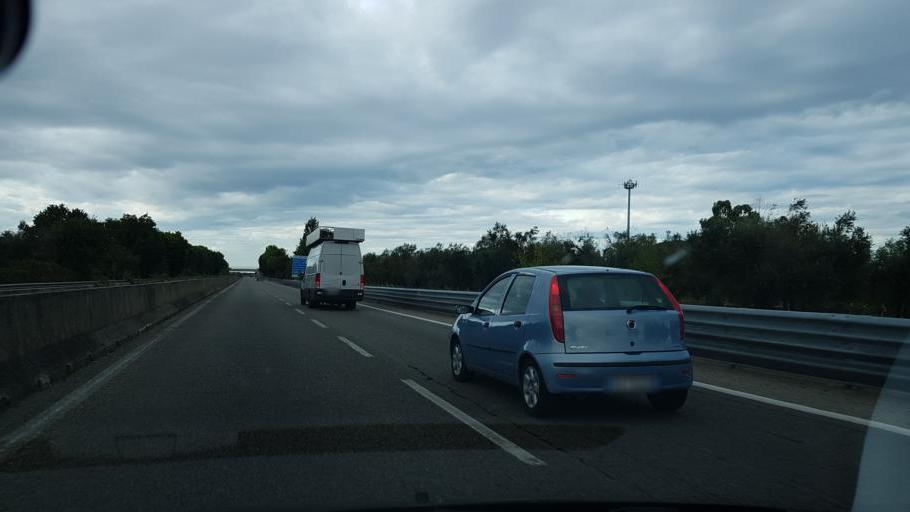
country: IT
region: Apulia
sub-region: Provincia di Brindisi
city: San Pietro Vernotico
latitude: 40.5146
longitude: 18.0218
